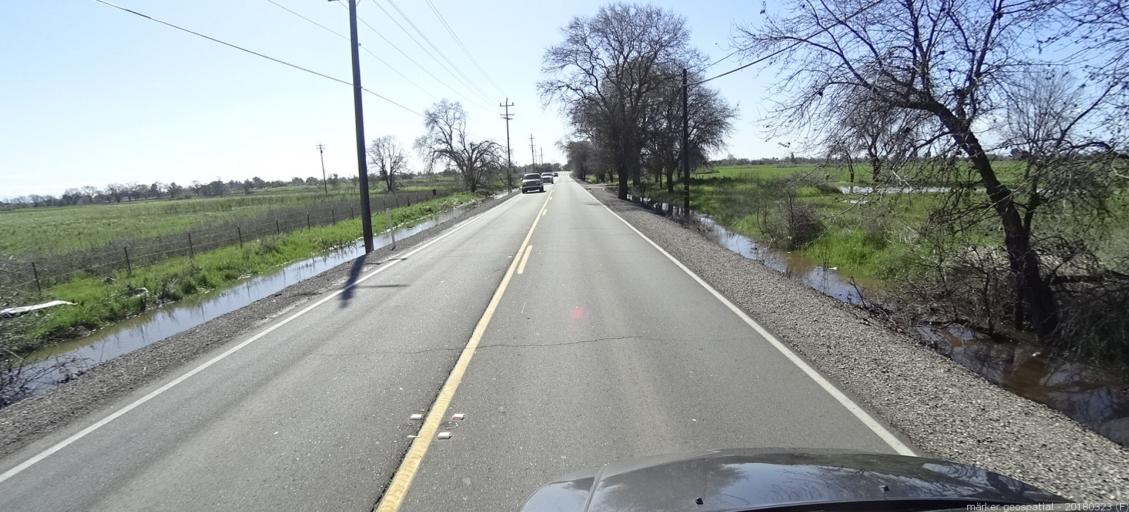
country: US
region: California
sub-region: Sacramento County
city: Rio Linda
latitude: 38.6699
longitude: -121.4538
